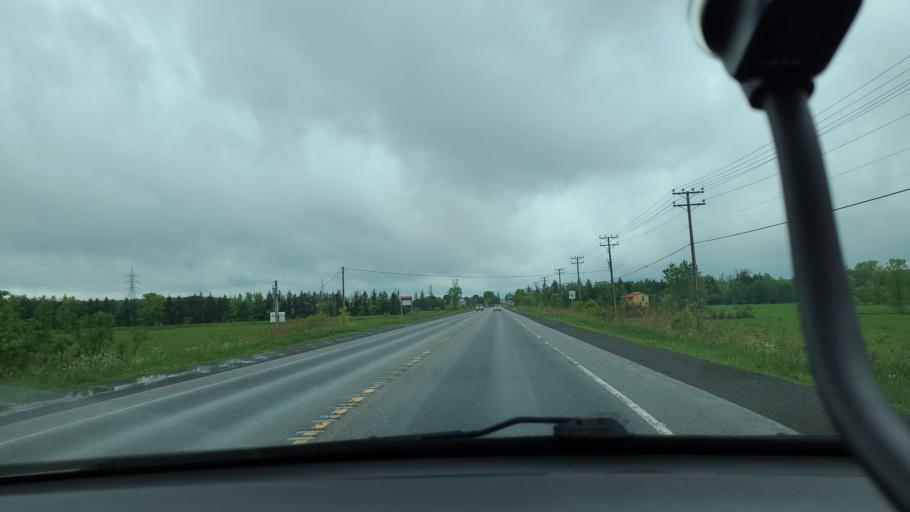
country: CA
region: Quebec
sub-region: Laurentides
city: Saint-Jerome
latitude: 45.7383
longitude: -74.0362
